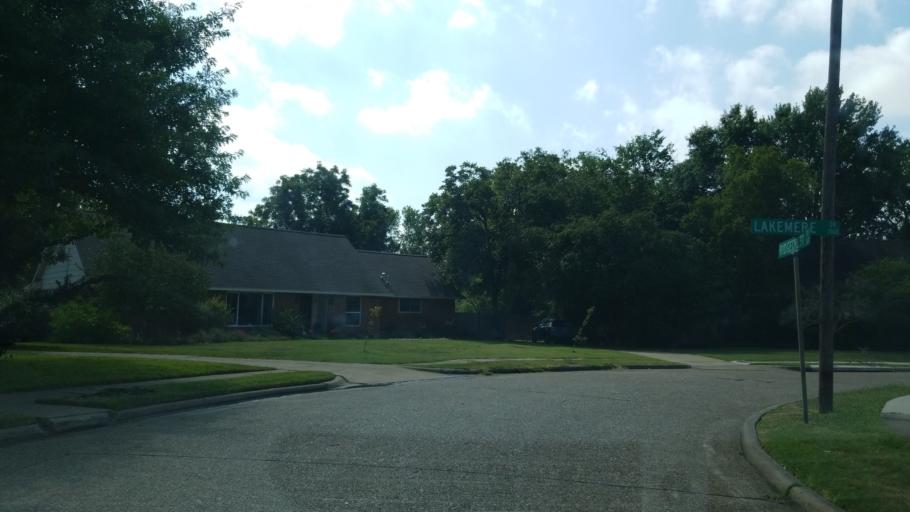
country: US
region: Texas
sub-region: Dallas County
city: Garland
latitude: 32.8914
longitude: -96.6575
